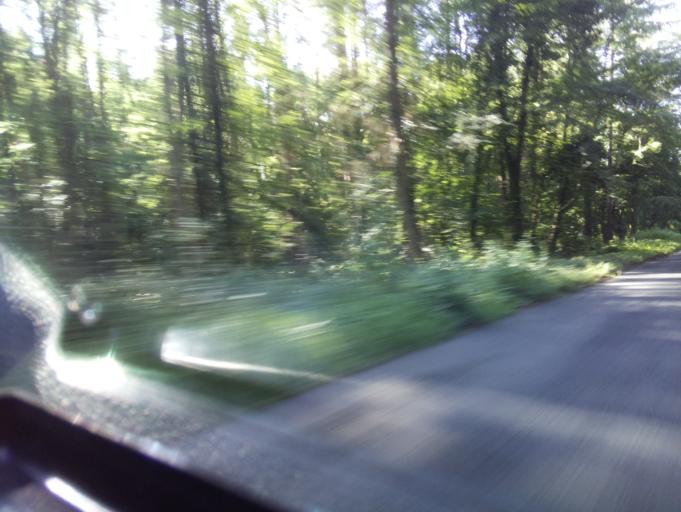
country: GB
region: Wales
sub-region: Monmouthshire
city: Tintern
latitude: 51.7220
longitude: -2.6916
